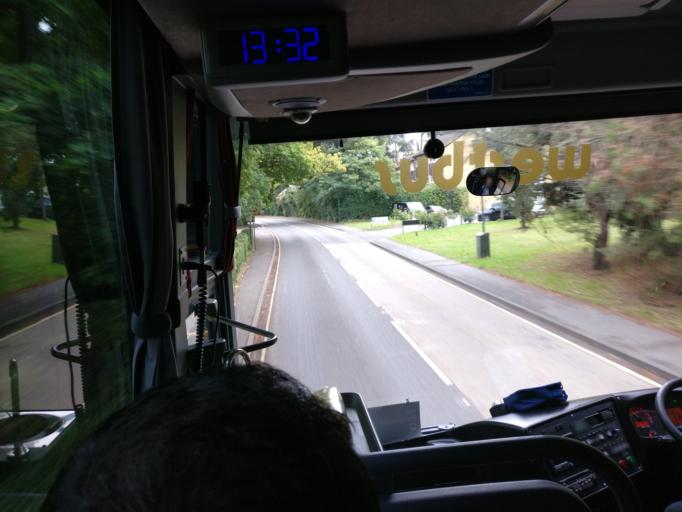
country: GB
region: England
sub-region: Surrey
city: Woking
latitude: 51.3256
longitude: -0.5618
